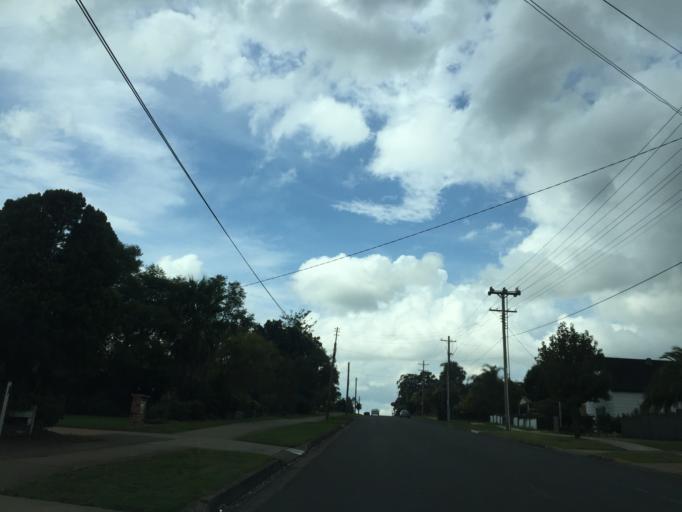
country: AU
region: New South Wales
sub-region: The Hills Shire
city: Beaumont Hills
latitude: -33.7128
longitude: 150.9626
